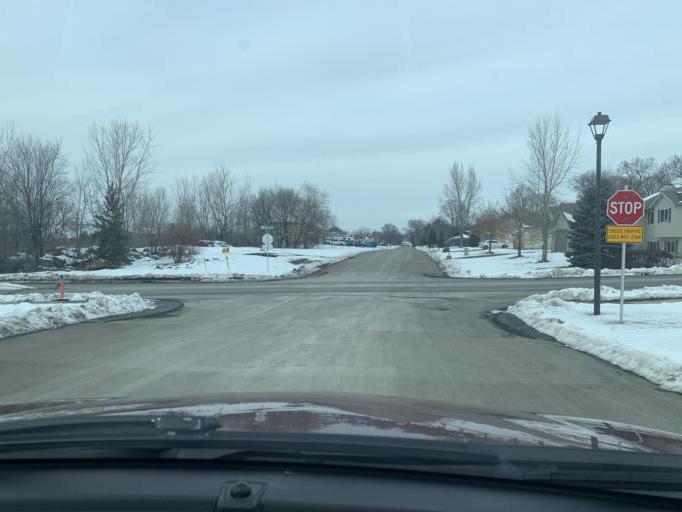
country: US
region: Minnesota
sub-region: Washington County
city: Saint Paul Park
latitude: 44.8420
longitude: -92.9929
